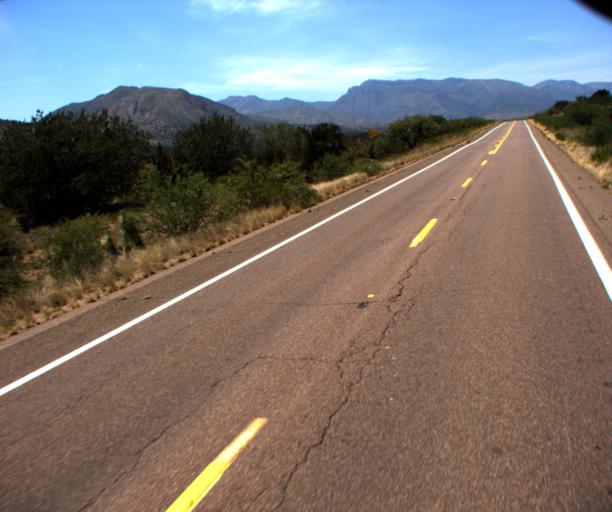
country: US
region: Arizona
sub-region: Gila County
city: Tonto Basin
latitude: 34.0148
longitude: -111.3264
